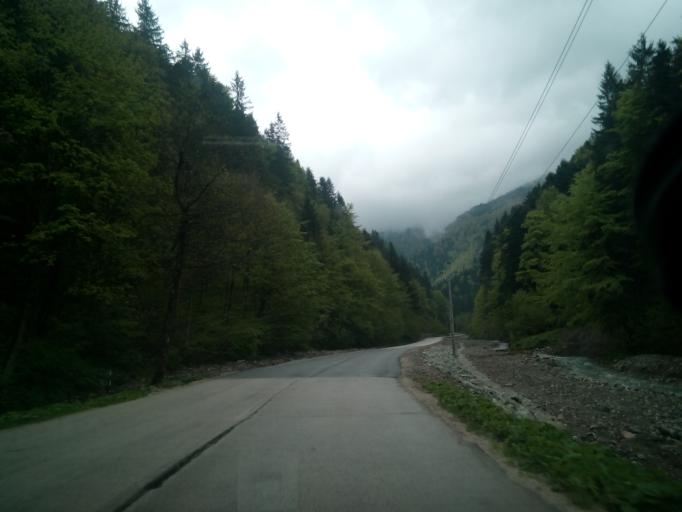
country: SK
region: Zilinsky
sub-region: Okres Zilina
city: Terchova
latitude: 49.2184
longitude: 19.0355
